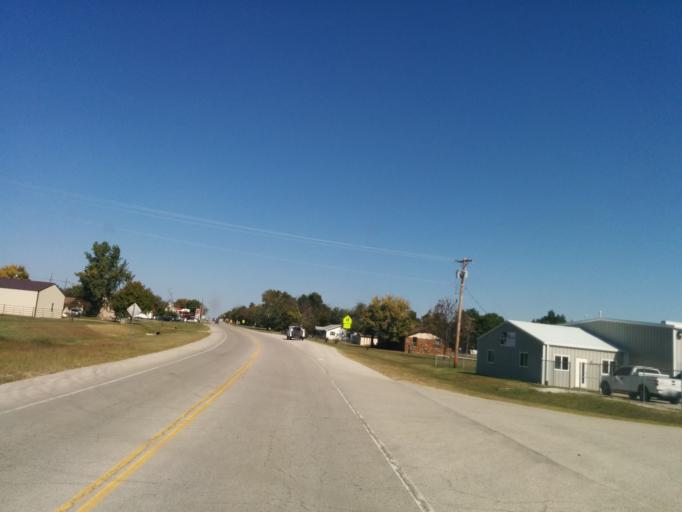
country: US
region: Oklahoma
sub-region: Creek County
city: Mounds
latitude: 35.8690
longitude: -96.0608
